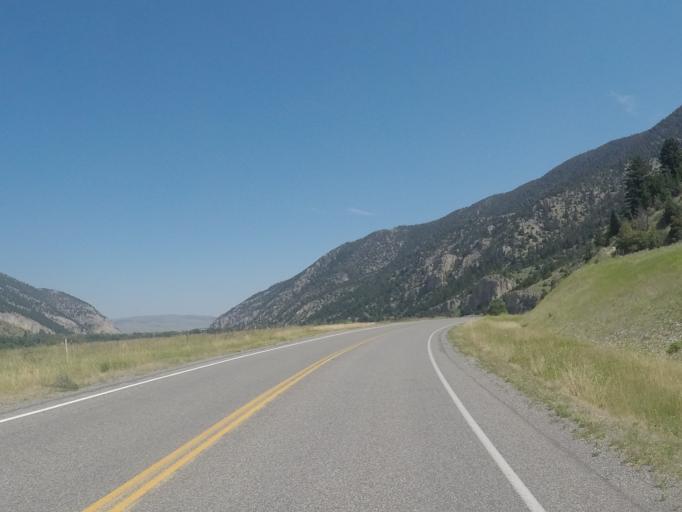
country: US
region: Montana
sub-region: Park County
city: Livingston
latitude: 45.5837
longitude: -110.5623
